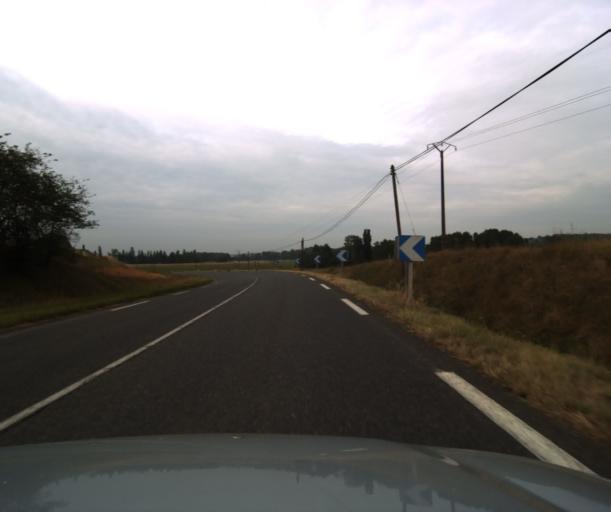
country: FR
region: Midi-Pyrenees
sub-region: Departement du Gers
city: Mirande
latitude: 43.5296
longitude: 0.4165
